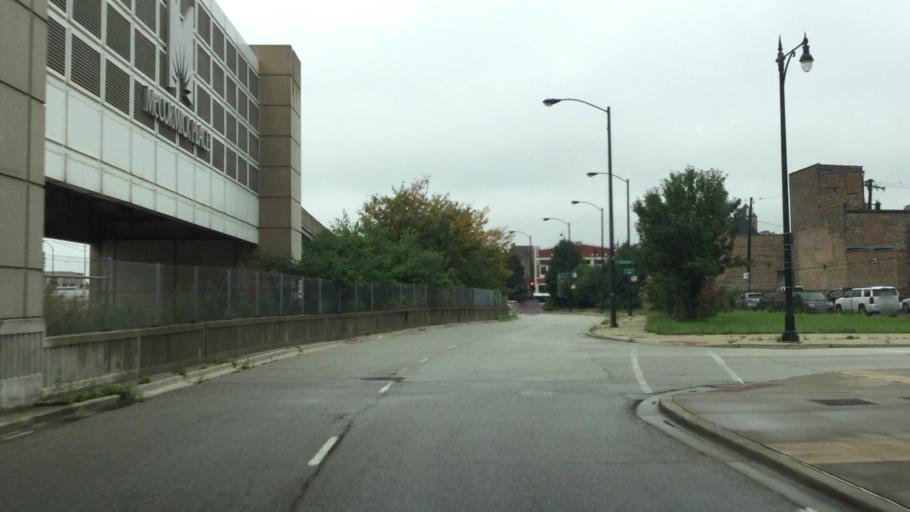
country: US
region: Illinois
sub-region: Cook County
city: Chicago
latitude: 41.8484
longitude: -87.6218
